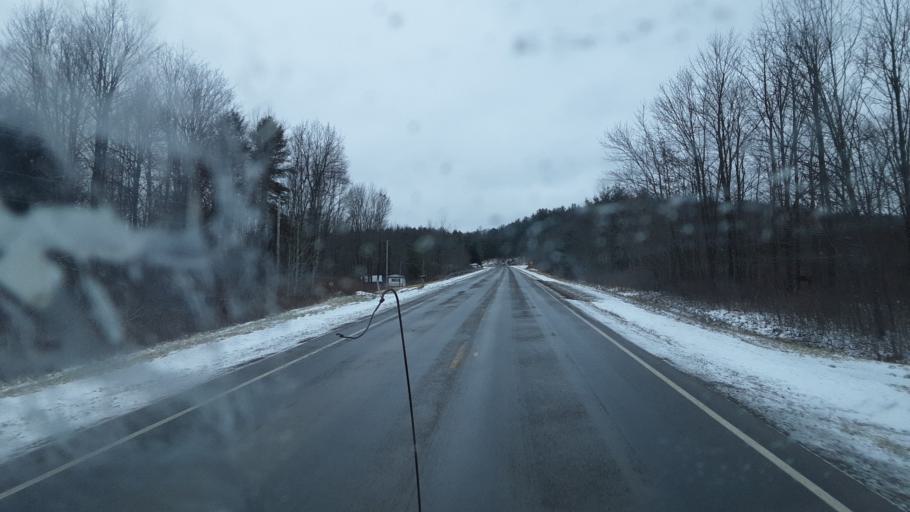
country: US
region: New York
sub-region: Allegany County
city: Friendship
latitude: 42.2174
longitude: -78.1442
